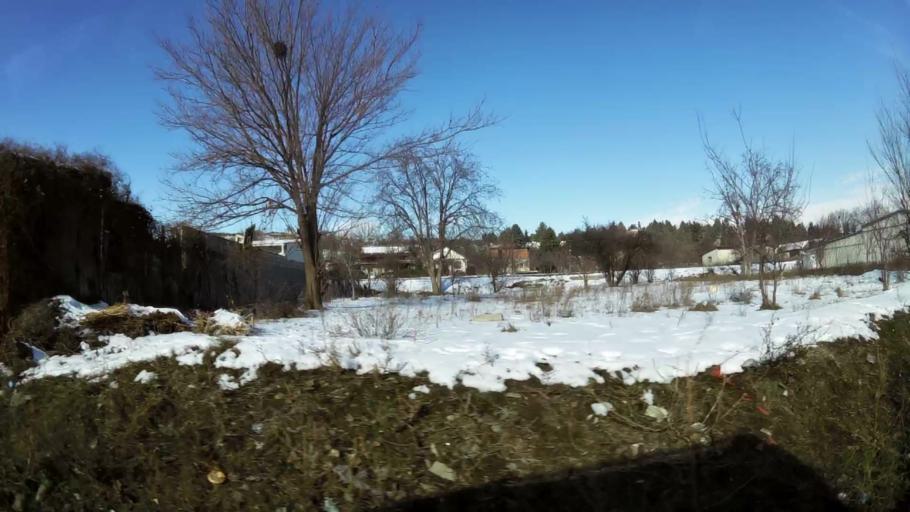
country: MK
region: Saraj
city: Saraj
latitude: 42.0105
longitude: 21.3424
